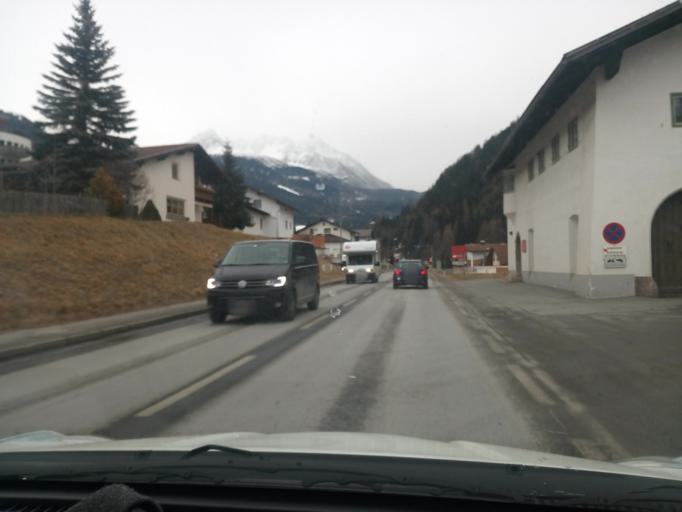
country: AT
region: Tyrol
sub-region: Politischer Bezirk Landeck
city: Nauders
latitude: 46.8903
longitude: 10.4994
